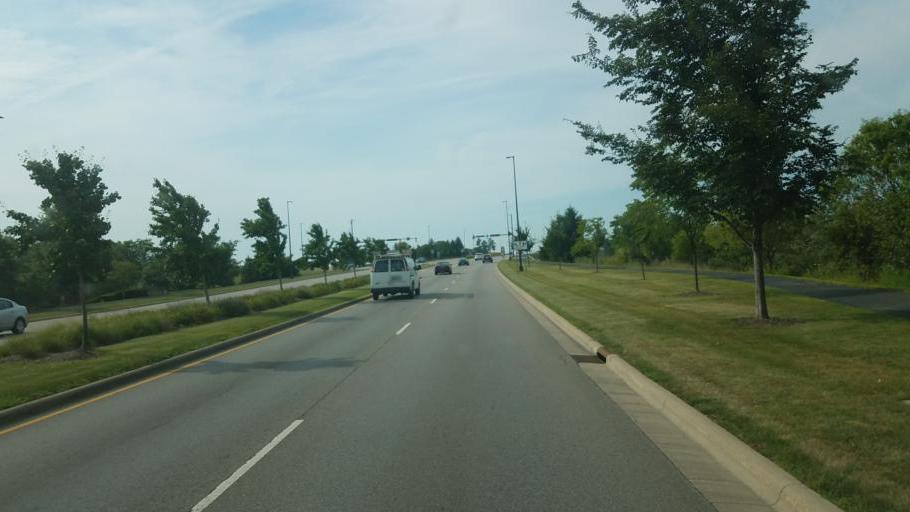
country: US
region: Ohio
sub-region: Franklin County
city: Dublin
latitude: 40.1023
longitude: -83.1597
